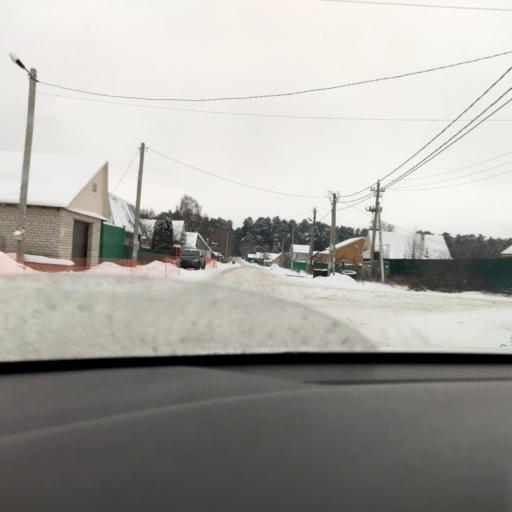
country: RU
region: Tatarstan
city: Osinovo
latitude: 55.8272
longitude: 48.8727
